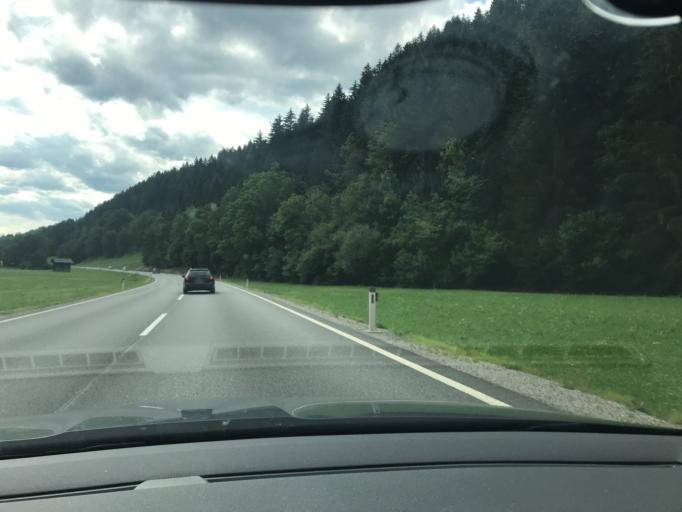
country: AT
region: Tyrol
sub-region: Politischer Bezirk Lienz
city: Abfaltersbach
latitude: 46.7605
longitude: 12.5525
